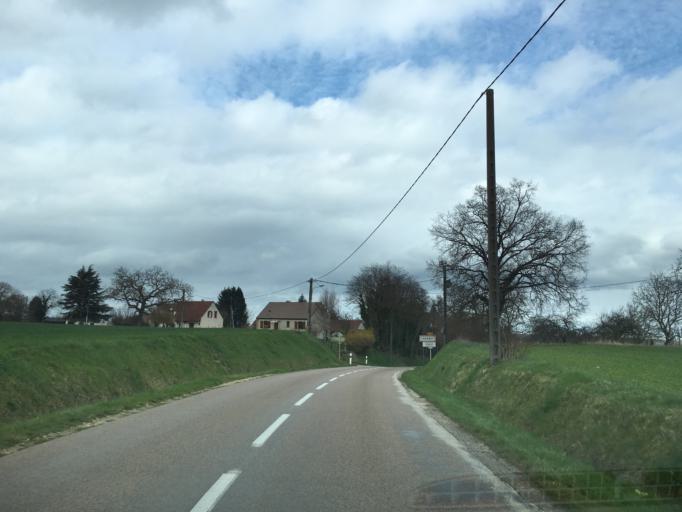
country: FR
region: Bourgogne
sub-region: Departement de l'Yonne
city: Charbuy
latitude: 47.8228
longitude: 3.4535
